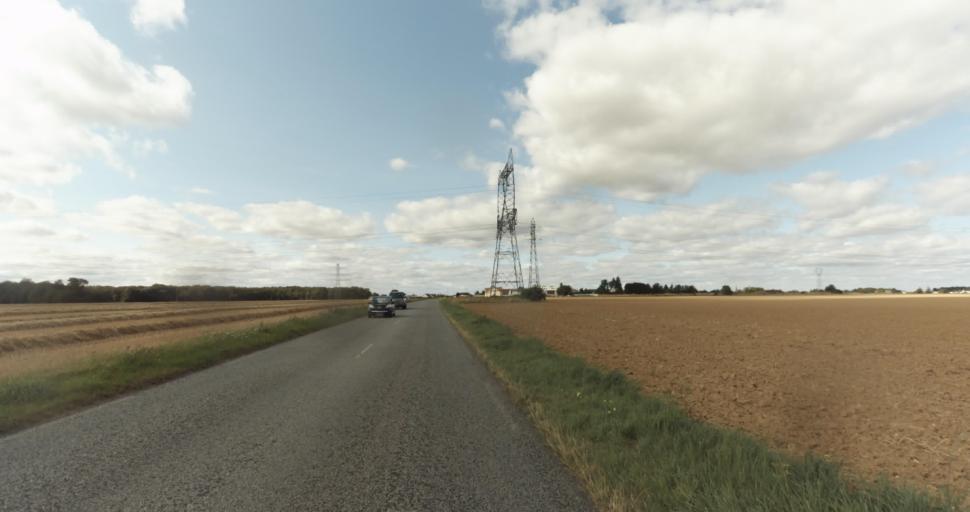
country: FR
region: Haute-Normandie
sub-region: Departement de l'Eure
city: La Couture-Boussey
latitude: 48.8863
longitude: 1.4059
